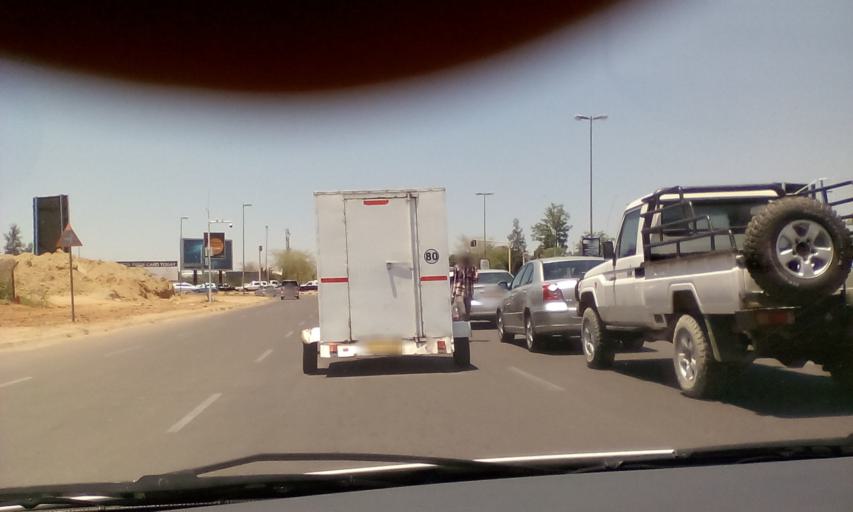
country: BW
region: South East
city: Gaborone
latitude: -24.6543
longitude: 25.9011
